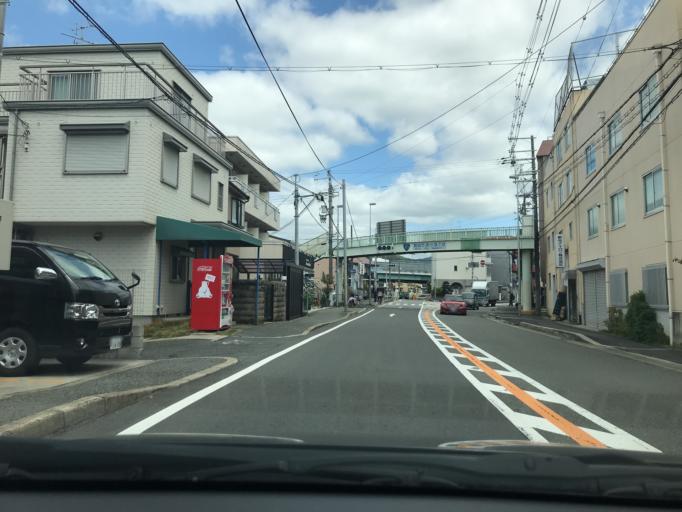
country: JP
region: Osaka
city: Ikeda
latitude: 34.8091
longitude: 135.4484
